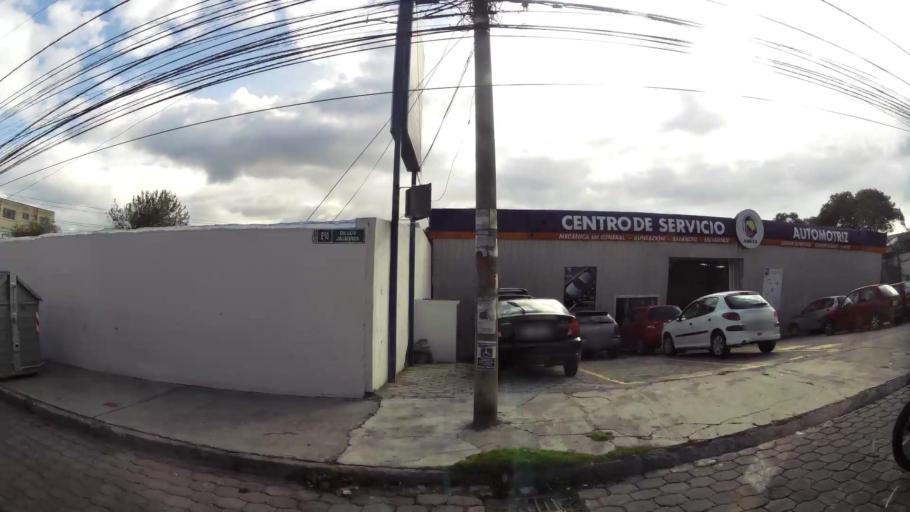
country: EC
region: Pichincha
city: Quito
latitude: -0.1352
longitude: -78.4715
